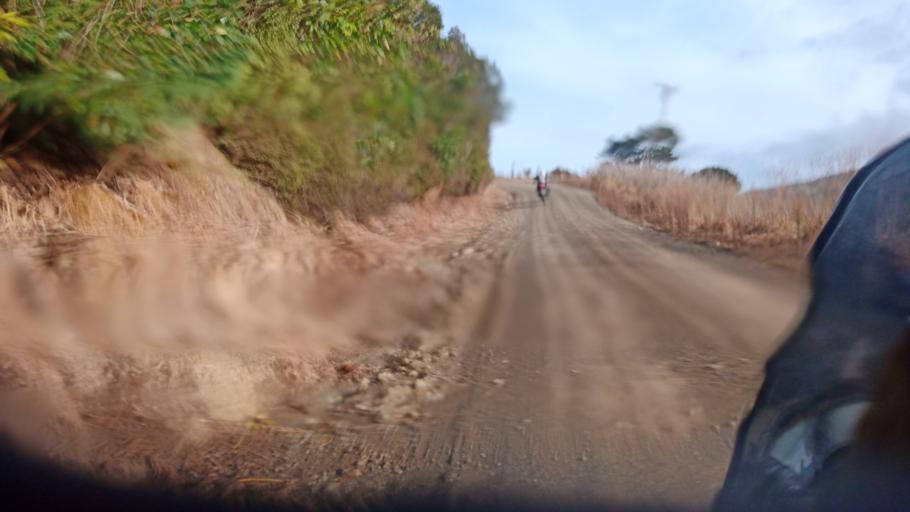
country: NZ
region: Bay of Plenty
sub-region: Opotiki District
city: Opotiki
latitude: -38.4456
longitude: 177.5382
